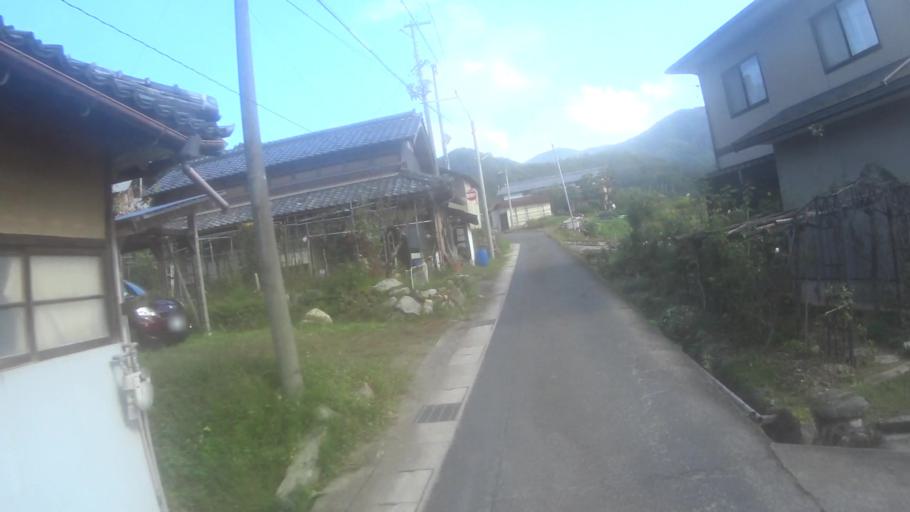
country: JP
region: Kyoto
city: Miyazu
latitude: 35.6099
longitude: 135.1481
